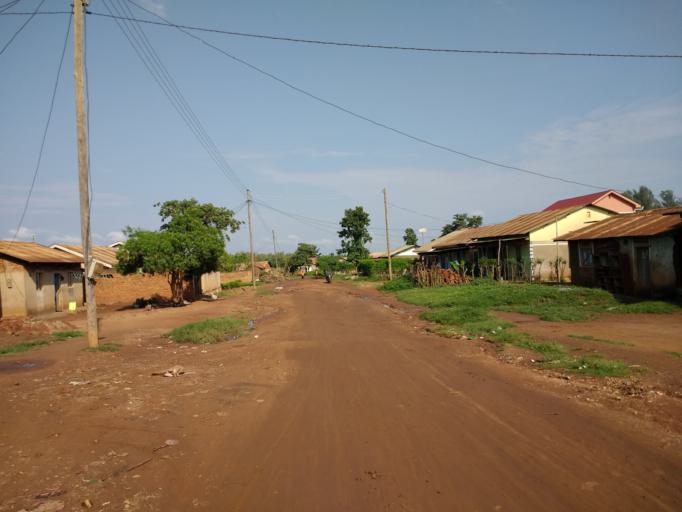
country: UG
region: Eastern Region
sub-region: Mbale District
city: Mbale
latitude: 1.0685
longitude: 34.1610
